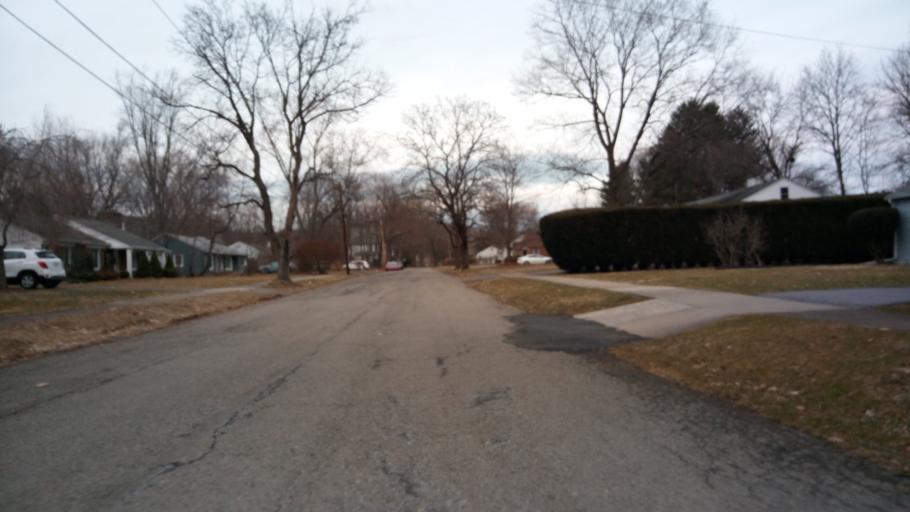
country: US
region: New York
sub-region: Chemung County
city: West Elmira
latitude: 42.0782
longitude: -76.8572
